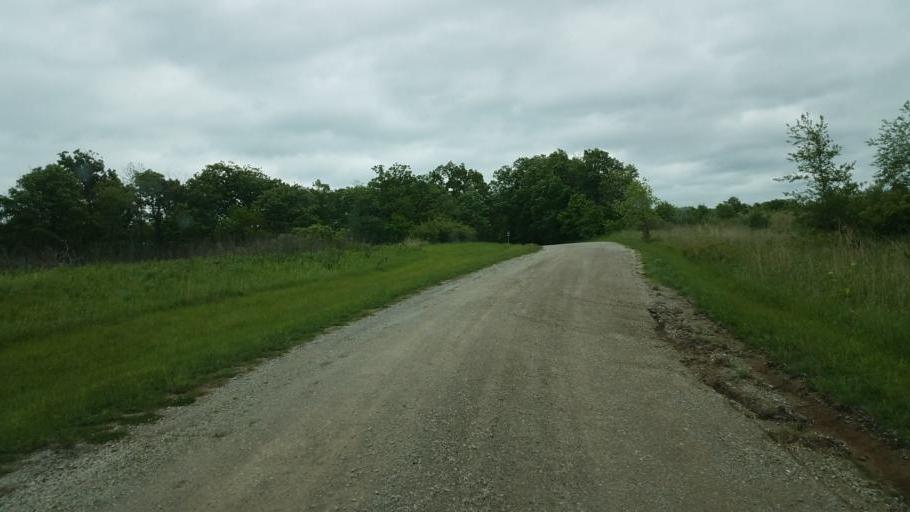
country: US
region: Iowa
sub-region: Decatur County
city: Lamoni
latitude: 40.6493
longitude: -93.8501
